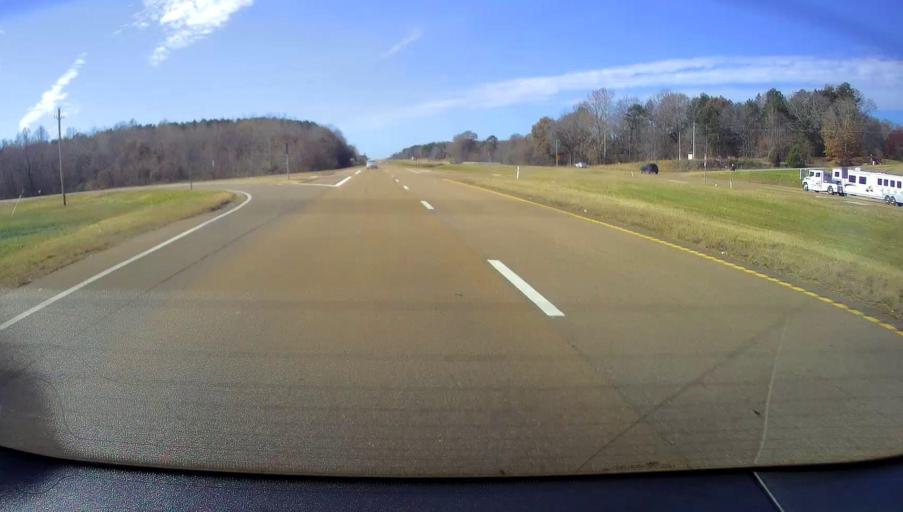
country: US
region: Mississippi
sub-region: Benton County
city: Ashland
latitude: 34.9521
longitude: -89.0584
